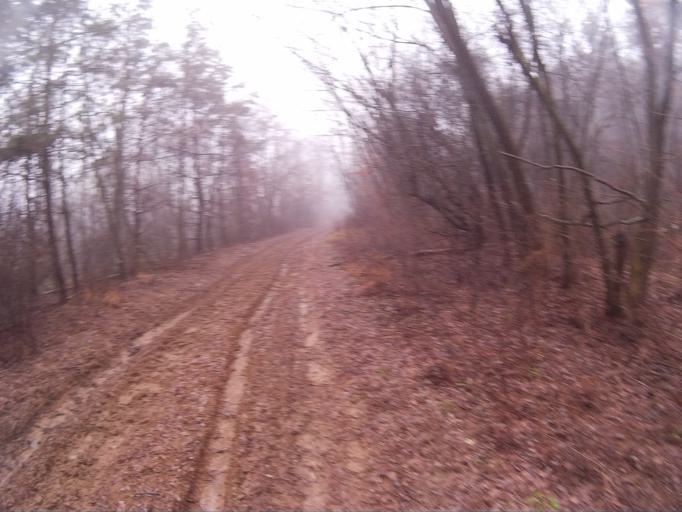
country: HU
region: Nograd
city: Somoskoujfalu
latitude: 48.1352
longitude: 19.8485
